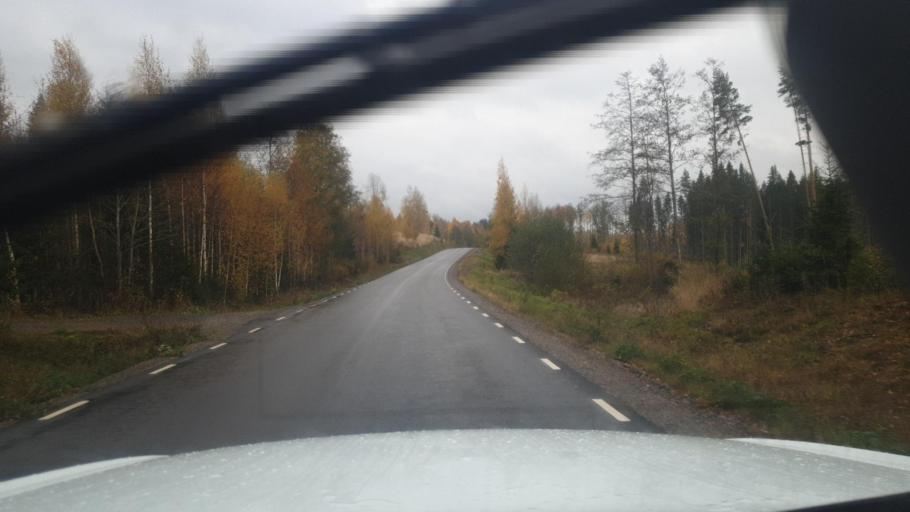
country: SE
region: Vaermland
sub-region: Torsby Kommun
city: Torsby
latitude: 59.9890
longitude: 12.7522
